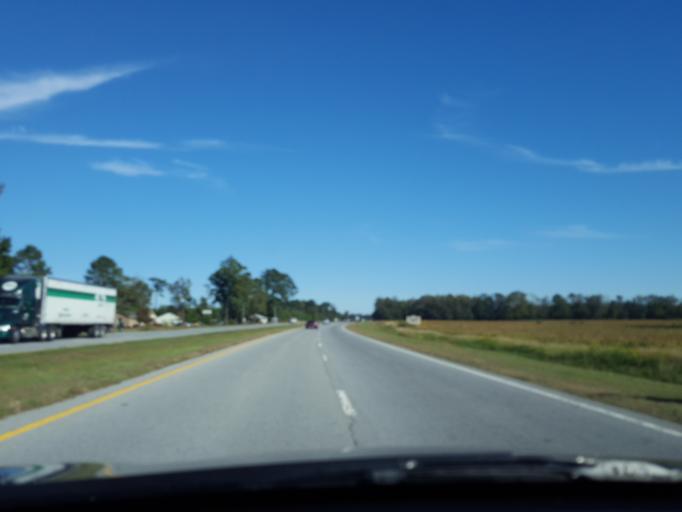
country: US
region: North Carolina
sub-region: Pitt County
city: Greenville
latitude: 35.6268
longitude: -77.2021
